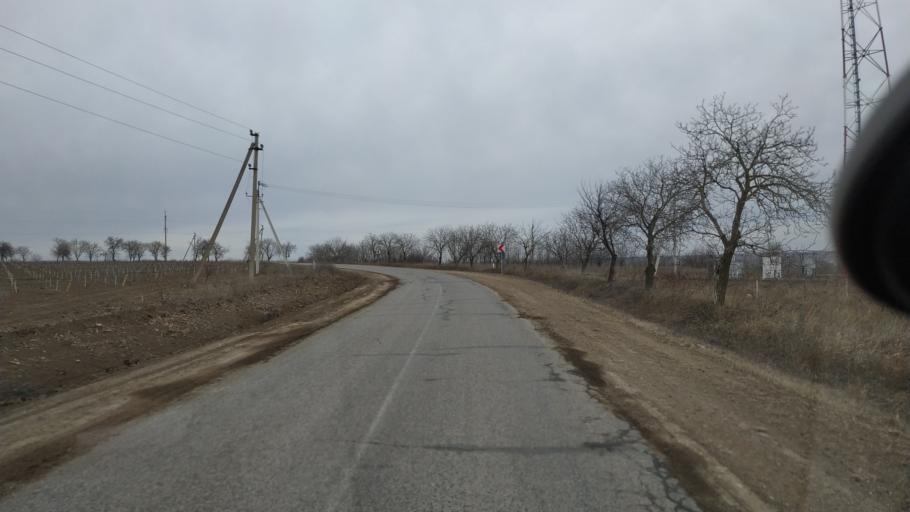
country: MD
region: Telenesti
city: Cocieri
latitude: 47.2680
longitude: 29.1142
